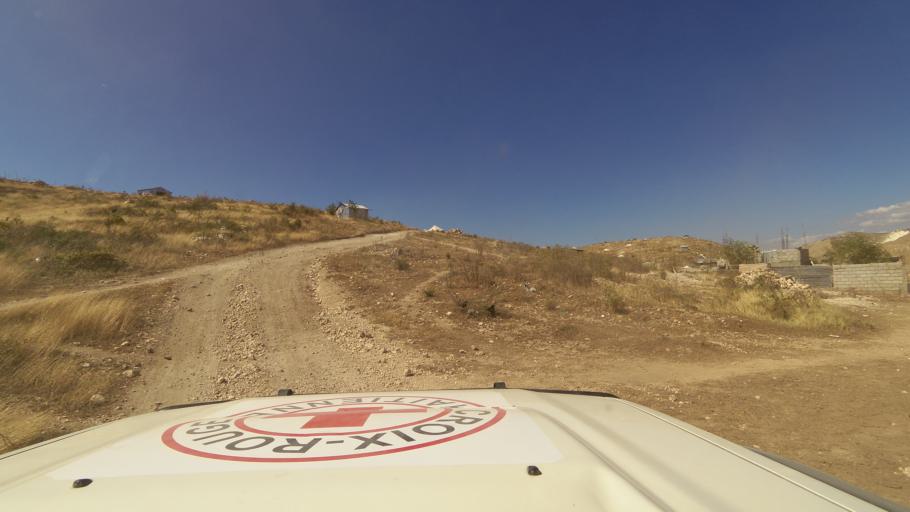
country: HT
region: Ouest
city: Croix des Bouquets
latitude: 18.6785
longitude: -72.2946
